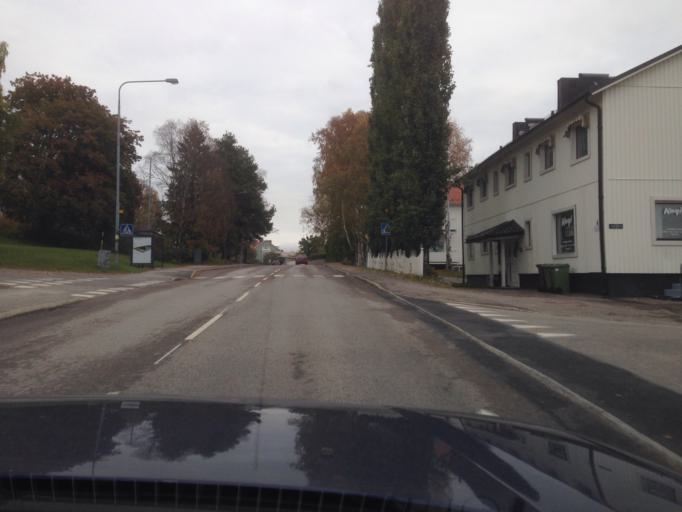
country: SE
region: Vaesternorrland
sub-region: Sundsvalls Kommun
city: Sundsvall
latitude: 62.3979
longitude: 17.3214
